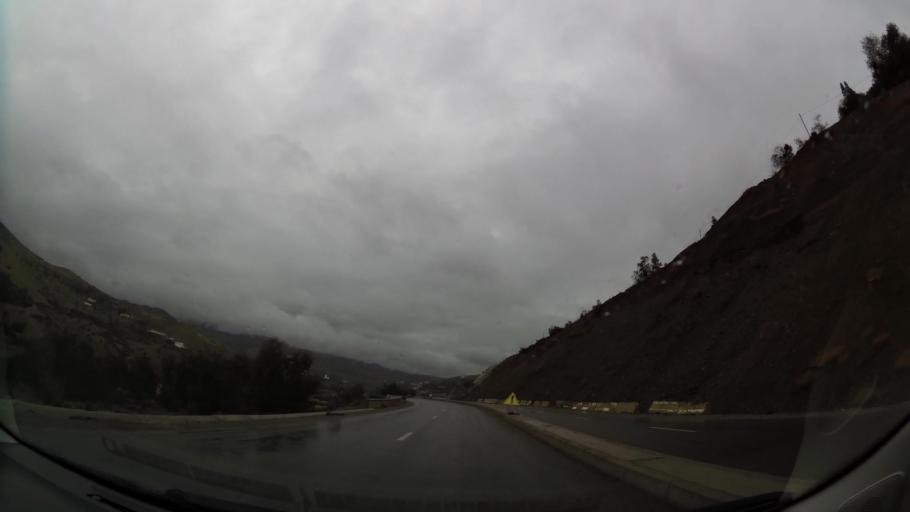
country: MA
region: Taza-Al Hoceima-Taounate
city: Imzourene
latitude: 35.0064
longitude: -3.8121
